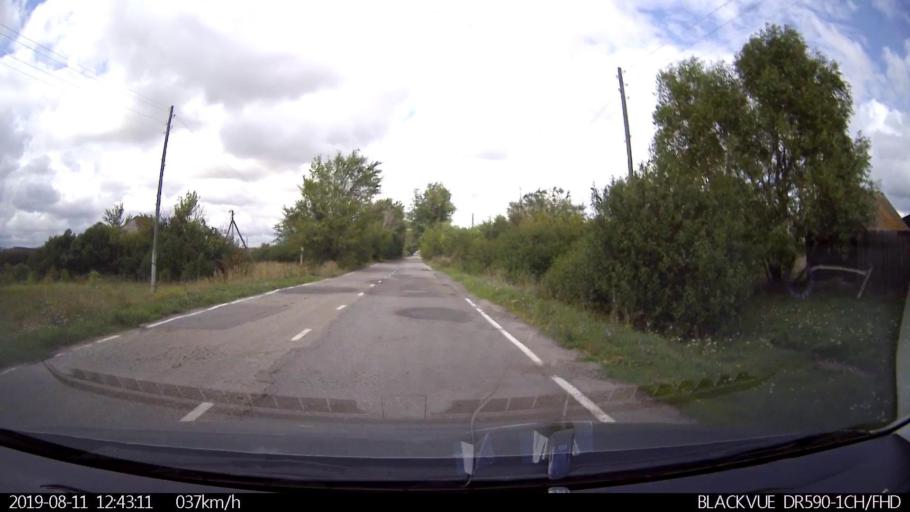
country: RU
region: Ulyanovsk
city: Ignatovka
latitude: 53.8498
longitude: 47.7446
